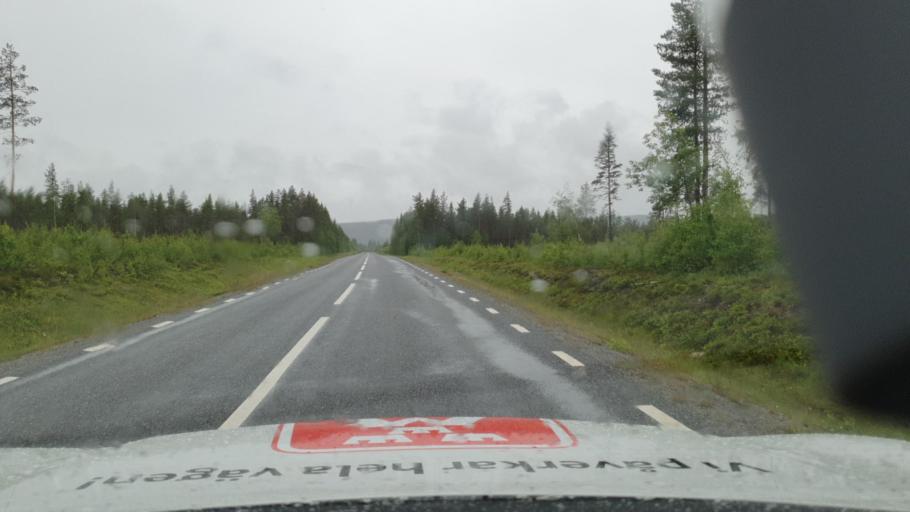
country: SE
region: Vaesterbotten
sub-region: Asele Kommun
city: Asele
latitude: 64.0703
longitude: 17.2880
